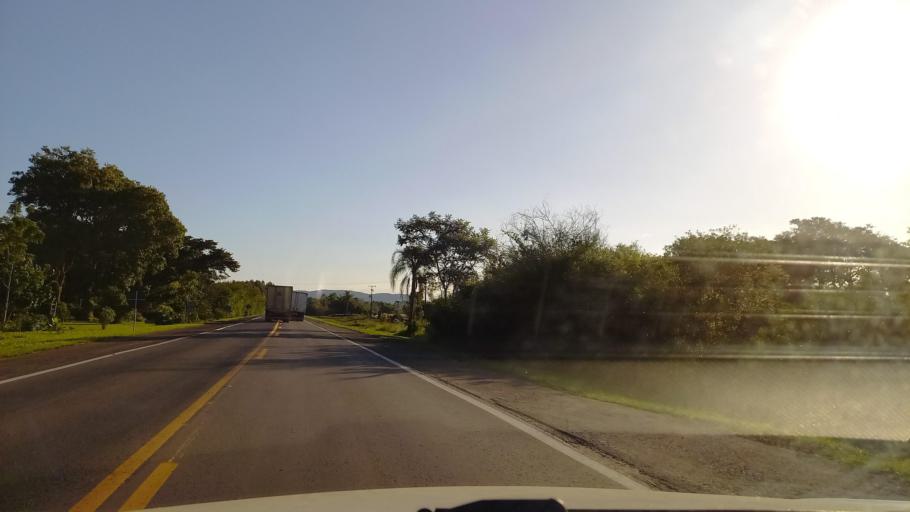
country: BR
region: Rio Grande do Sul
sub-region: Venancio Aires
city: Venancio Aires
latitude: -29.6683
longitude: -52.0315
